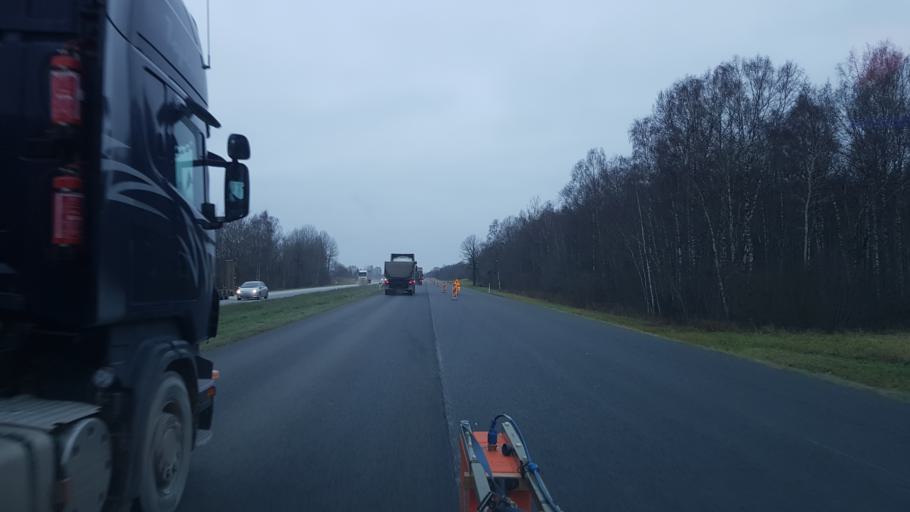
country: EE
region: Harju
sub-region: Rae vald
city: Jueri
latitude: 59.3317
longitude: 24.9145
